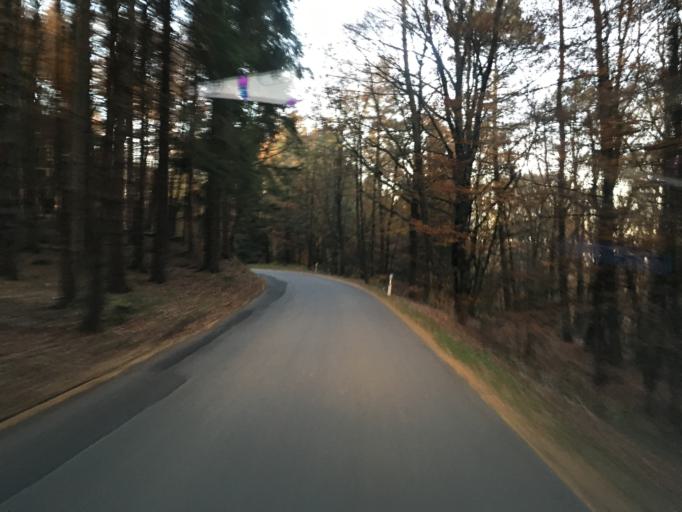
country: DE
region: North Rhine-Westphalia
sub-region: Regierungsbezirk Arnsberg
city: Luedenscheid
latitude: 51.2667
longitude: 7.6091
